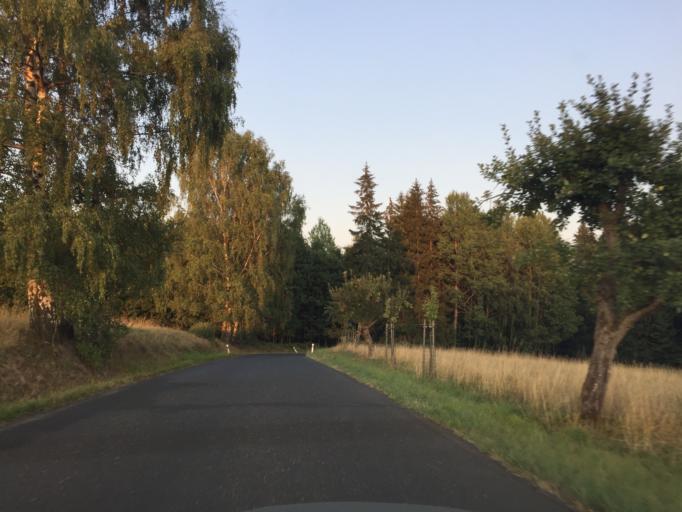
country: CZ
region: Ustecky
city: Ceska Kamenice
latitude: 50.8557
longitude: 14.3679
